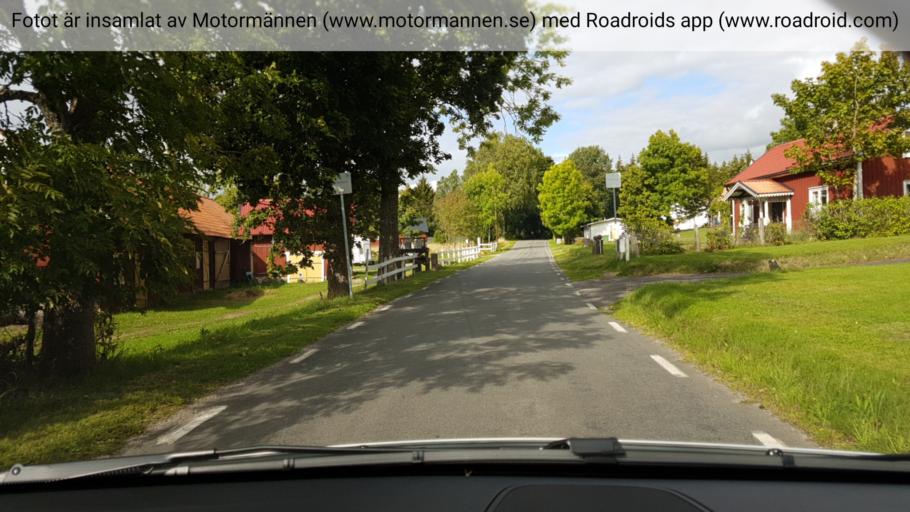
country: SE
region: Vaestra Goetaland
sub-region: Skovde Kommun
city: Skultorp
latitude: 58.2980
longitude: 13.8334
